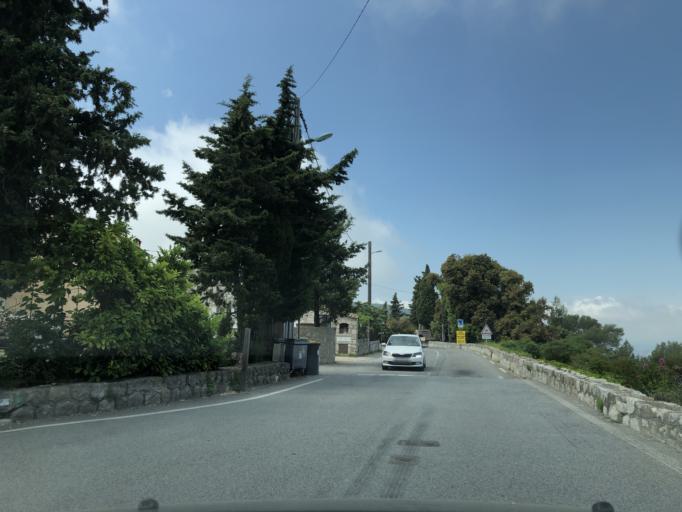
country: FR
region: Provence-Alpes-Cote d'Azur
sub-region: Departement des Alpes-Maritimes
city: Eze
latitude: 43.7341
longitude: 7.3466
